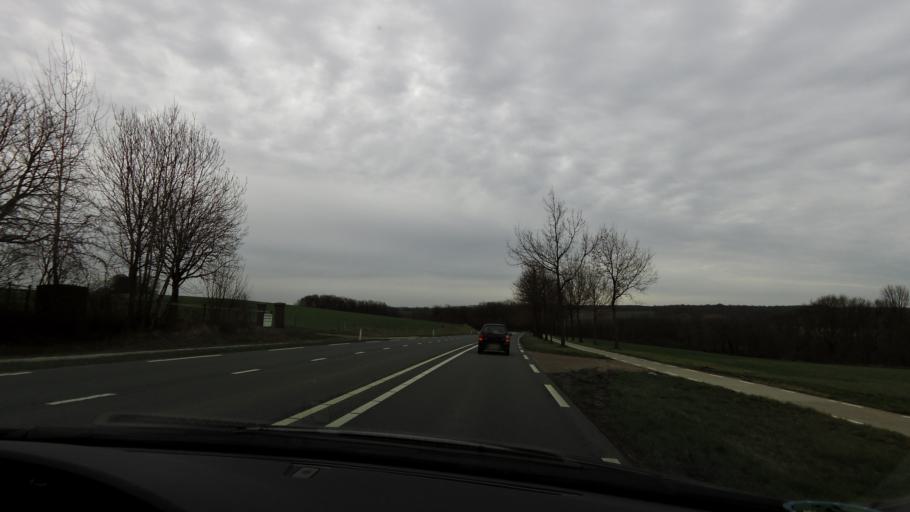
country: NL
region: Limburg
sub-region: Valkenburg aan de Geul
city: Schin op Geul
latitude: 50.8120
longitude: 5.8665
